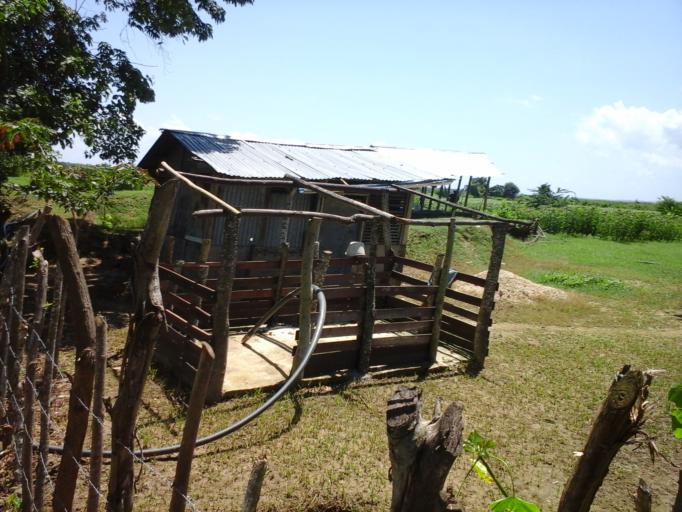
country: CO
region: Bolivar
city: Mahates
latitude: 10.1622
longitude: -75.2747
